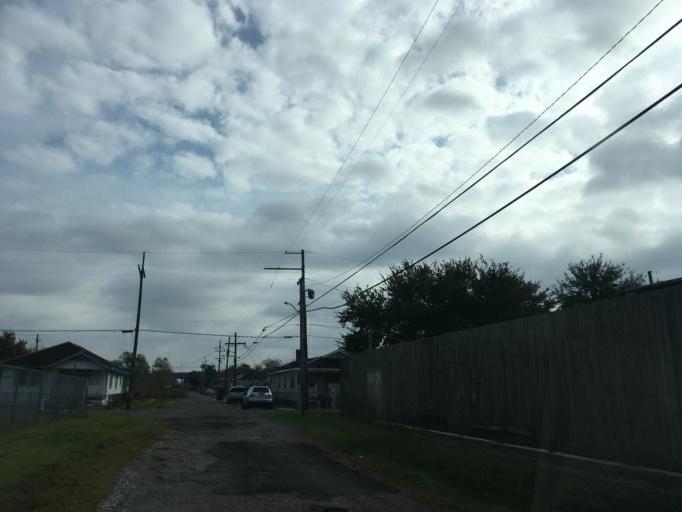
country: US
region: Louisiana
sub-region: Orleans Parish
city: New Orleans
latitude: 29.9879
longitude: -90.0575
